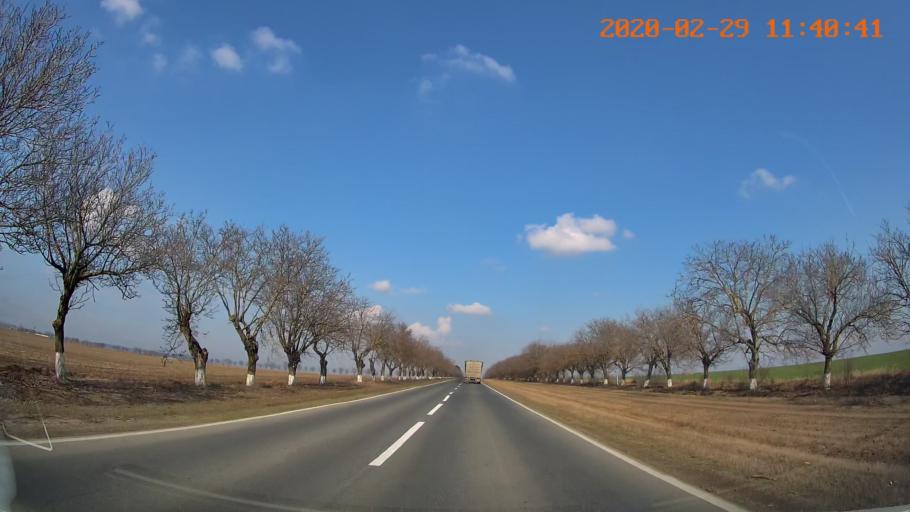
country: MD
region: Rezina
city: Saharna
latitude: 47.6600
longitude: 29.0193
